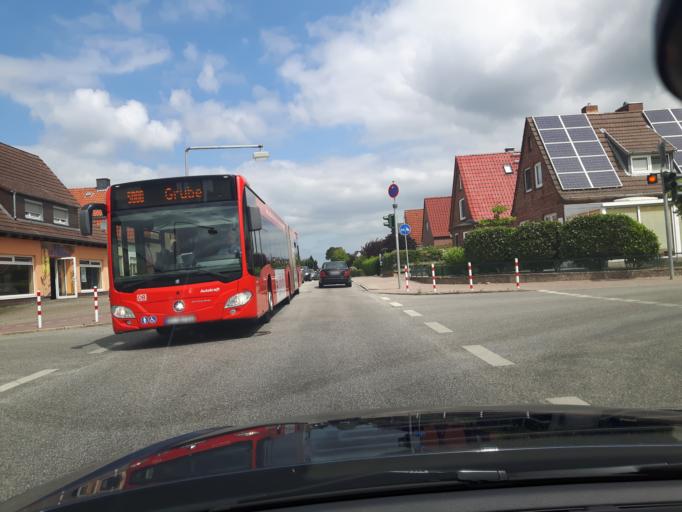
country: DE
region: Schleswig-Holstein
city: Neustadt in Holstein
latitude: 54.1010
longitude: 10.8213
